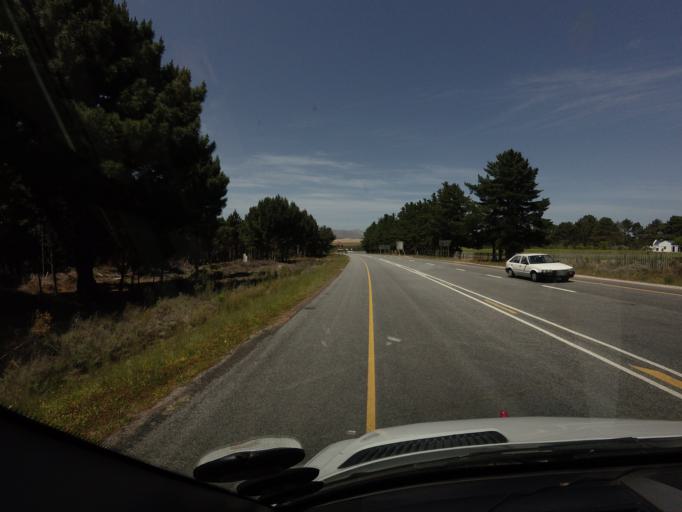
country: ZA
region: Western Cape
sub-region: Overberg District Municipality
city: Hermanus
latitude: -34.3006
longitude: 19.1437
